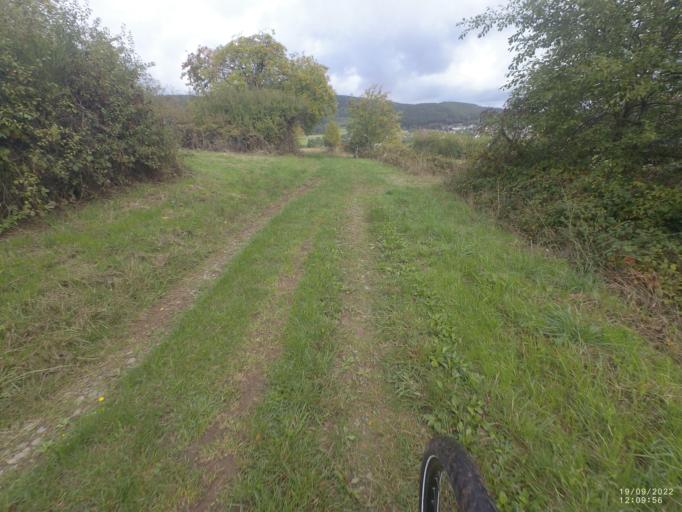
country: DE
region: Rheinland-Pfalz
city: Wallenborn
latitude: 50.1468
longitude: 6.7113
